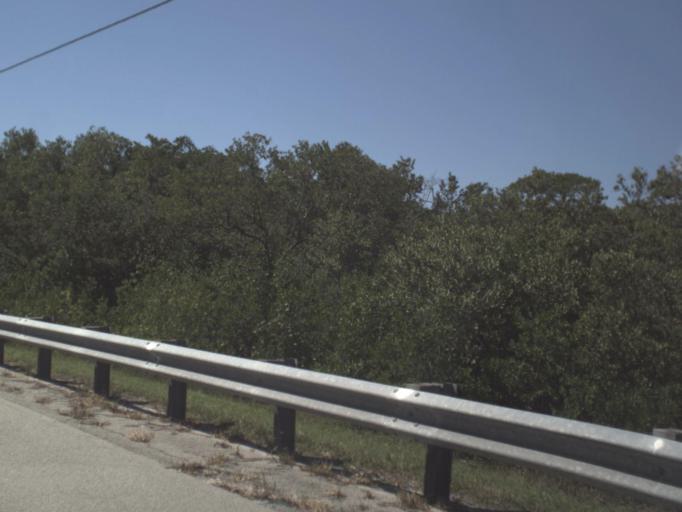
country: US
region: Florida
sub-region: Collier County
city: Marco
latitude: 25.9701
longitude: -81.7078
